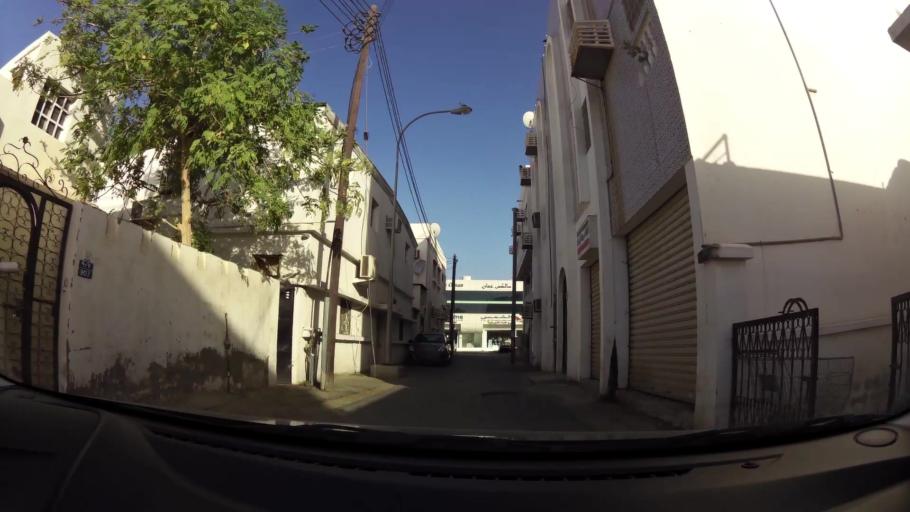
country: OM
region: Muhafazat Masqat
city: Muscat
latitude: 23.5881
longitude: 58.5511
